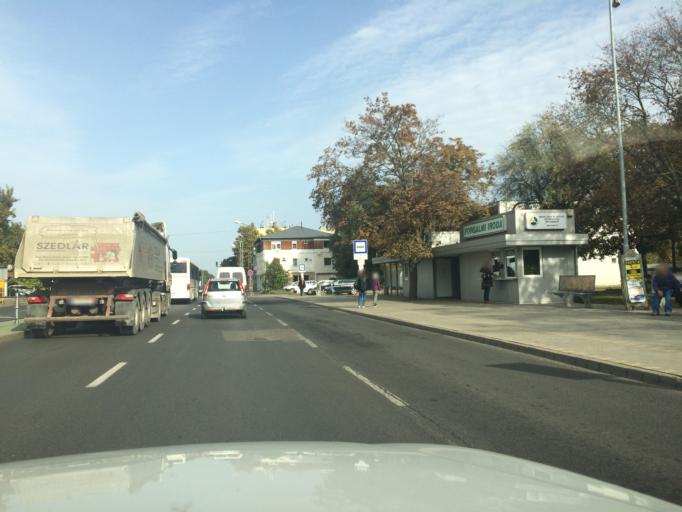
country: HU
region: Szabolcs-Szatmar-Bereg
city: Nyiregyhaza
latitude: 47.9471
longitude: 21.7066
